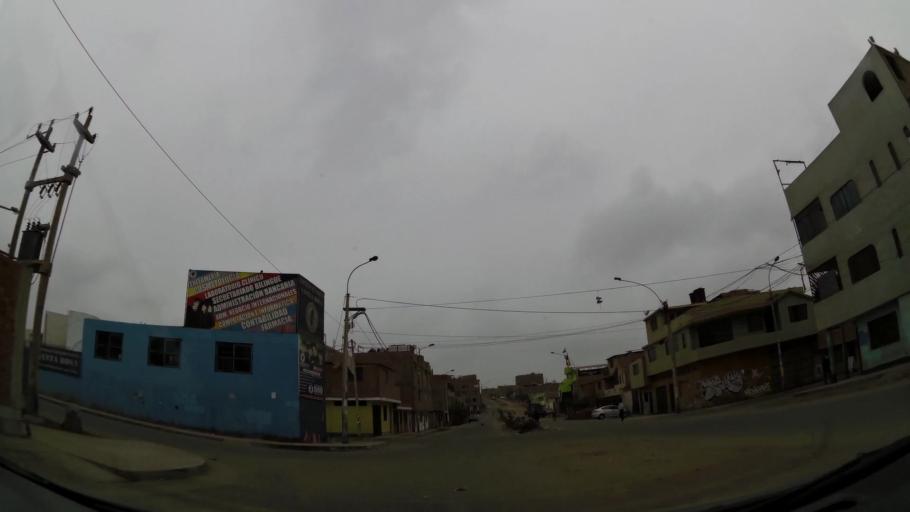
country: PE
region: Lima
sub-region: Lima
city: Surco
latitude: -12.1886
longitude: -76.9794
